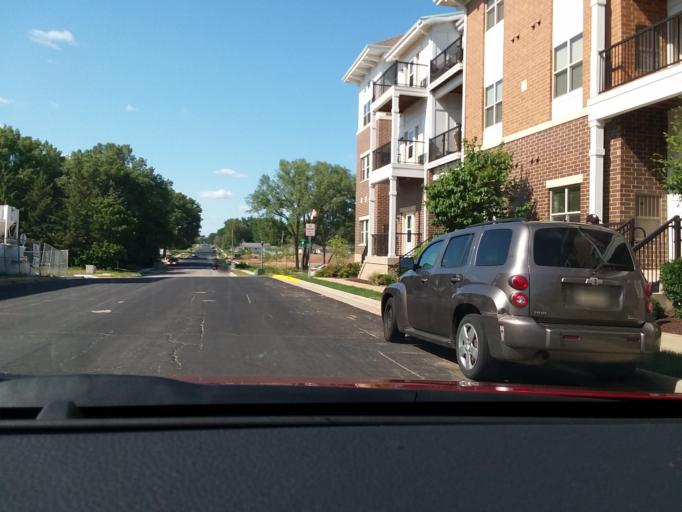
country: US
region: Wisconsin
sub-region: Dane County
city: Waunakee
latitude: 43.1924
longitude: -89.4518
